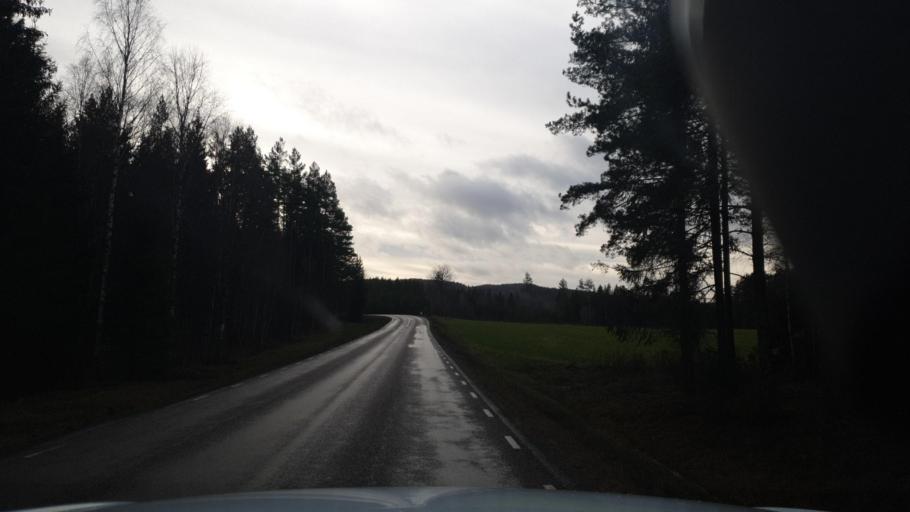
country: SE
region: Vaermland
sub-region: Eda Kommun
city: Amotfors
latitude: 59.7338
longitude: 12.1698
